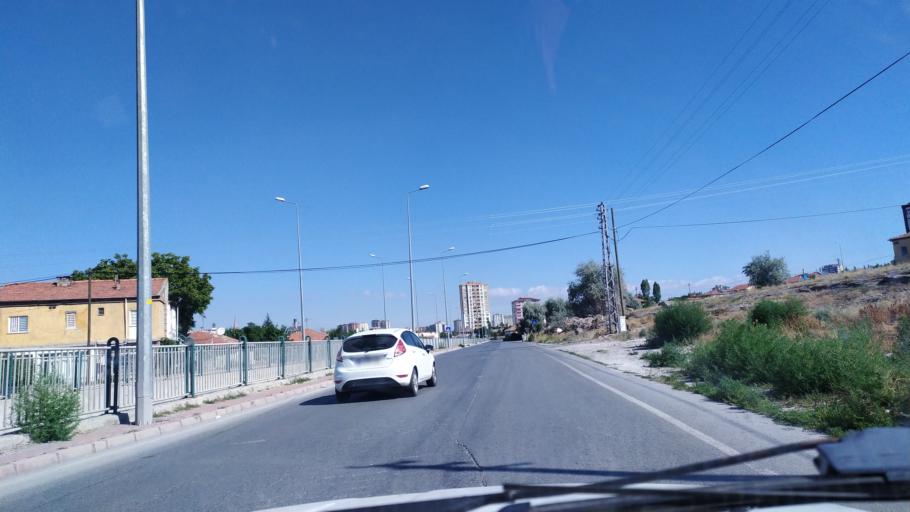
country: TR
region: Kayseri
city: Talas
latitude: 38.7240
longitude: 35.5505
